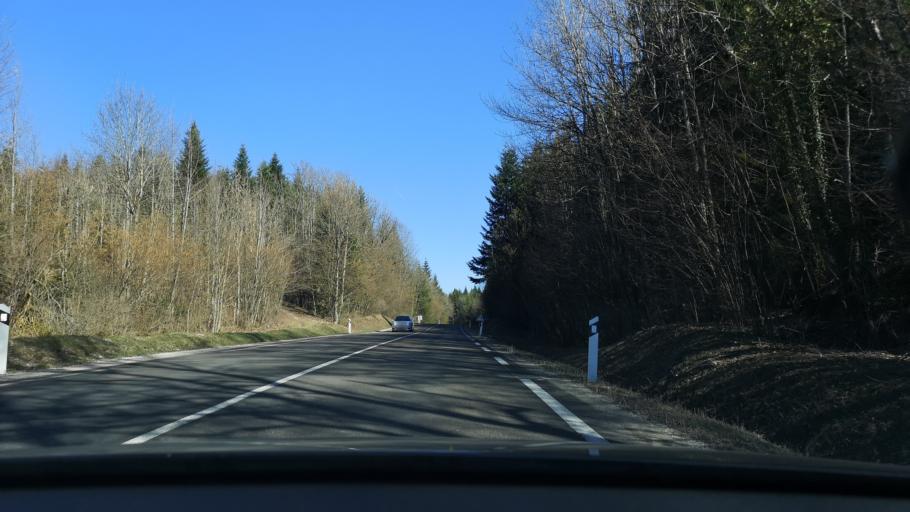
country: FR
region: Franche-Comte
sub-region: Departement du Doubs
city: Doubs
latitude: 46.9685
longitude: 6.3450
